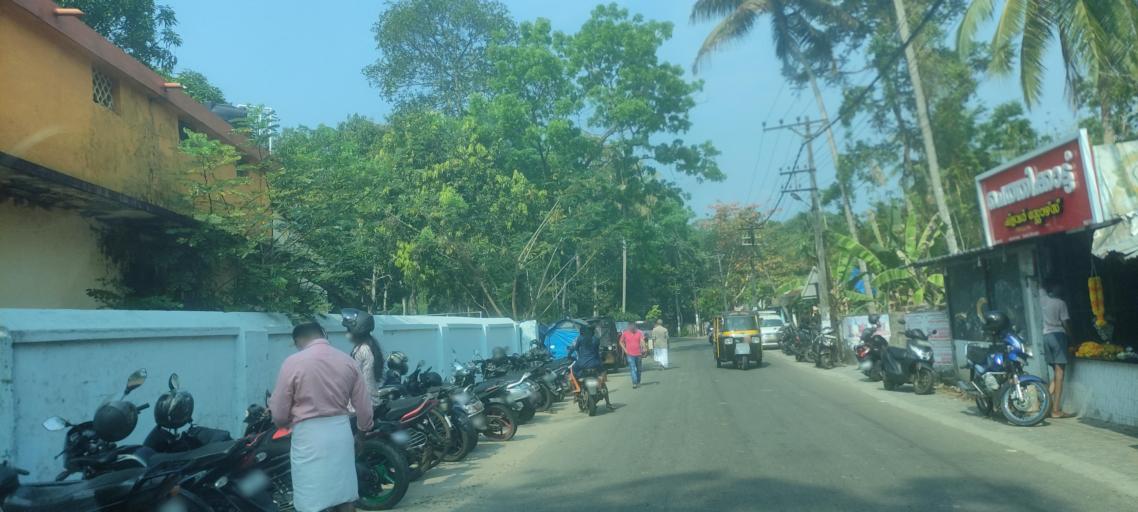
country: IN
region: Kerala
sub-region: Alappuzha
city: Kutiatodu
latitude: 9.7686
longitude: 76.3170
